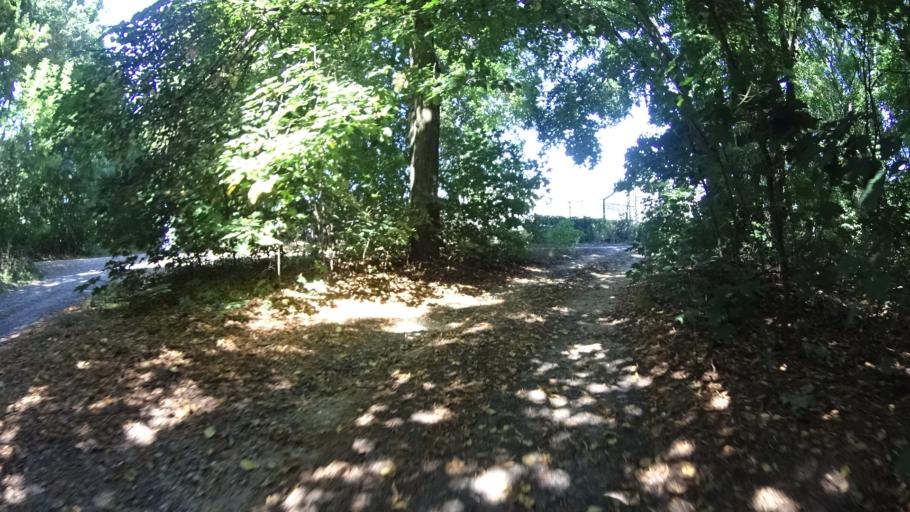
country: PL
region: Masovian Voivodeship
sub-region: Powiat bialobrzeski
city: Bialobrzegi
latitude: 51.6700
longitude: 20.9296
